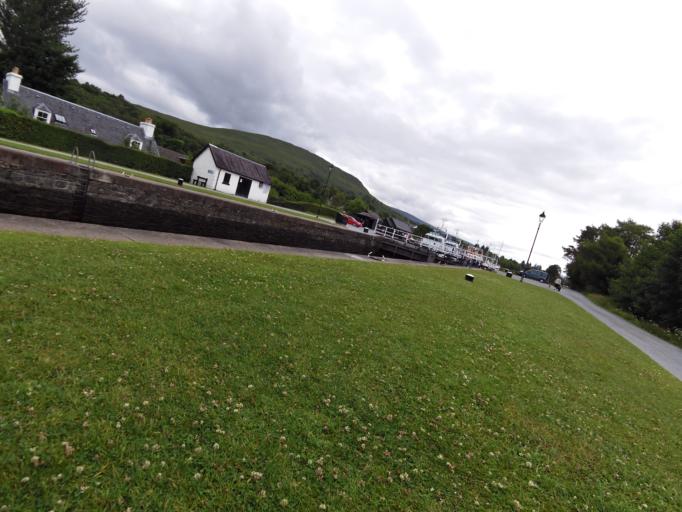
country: GB
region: Scotland
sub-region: Highland
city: Fort William
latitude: 56.8473
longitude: -5.0920
